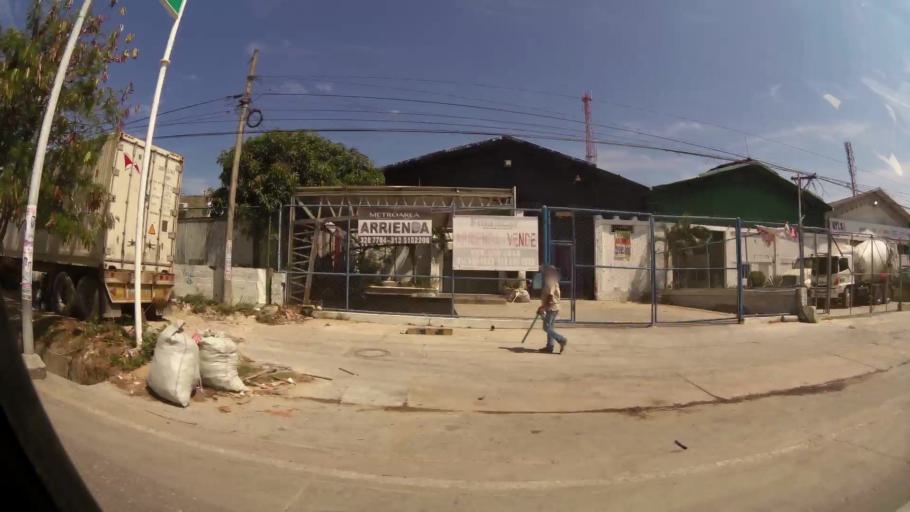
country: CO
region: Atlantico
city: Barranquilla
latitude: 10.9798
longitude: -74.8360
